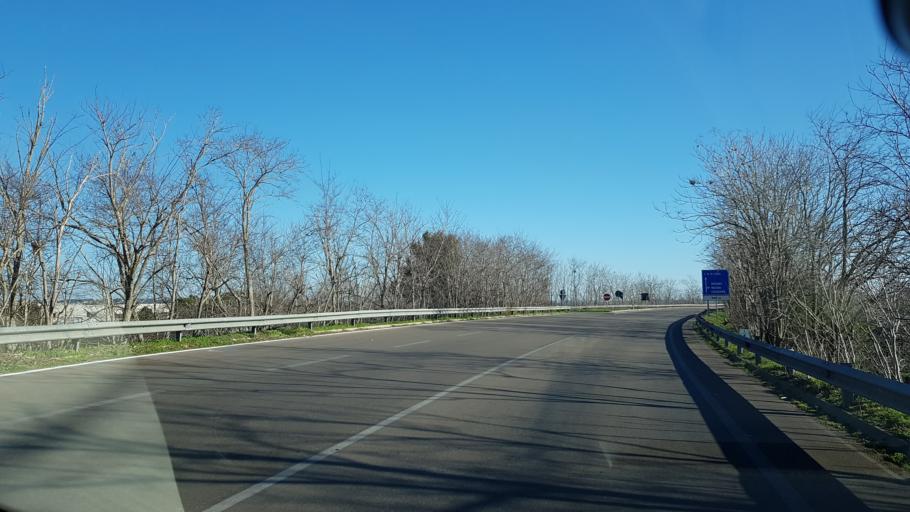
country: IT
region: Apulia
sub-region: Provincia di Lecce
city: Taviano
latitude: 39.9947
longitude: 18.0972
